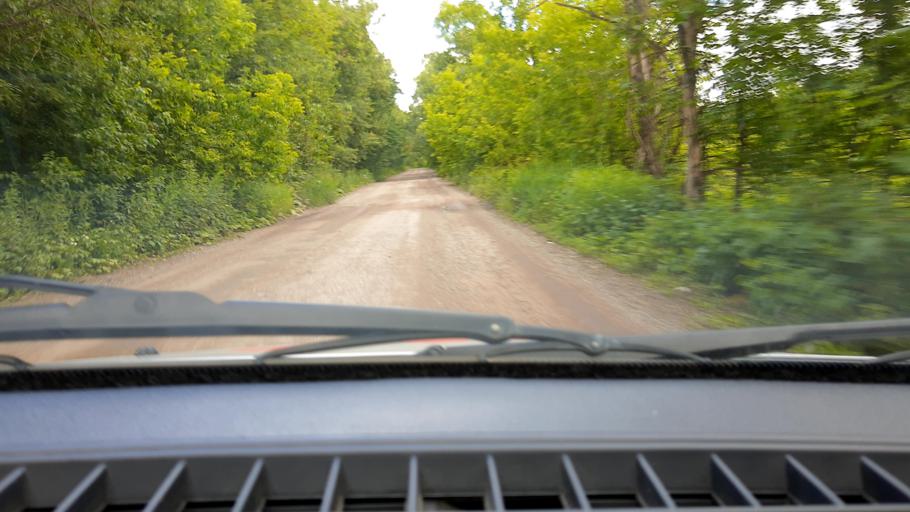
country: RU
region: Bashkortostan
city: Ufa
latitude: 54.6792
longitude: 56.0609
